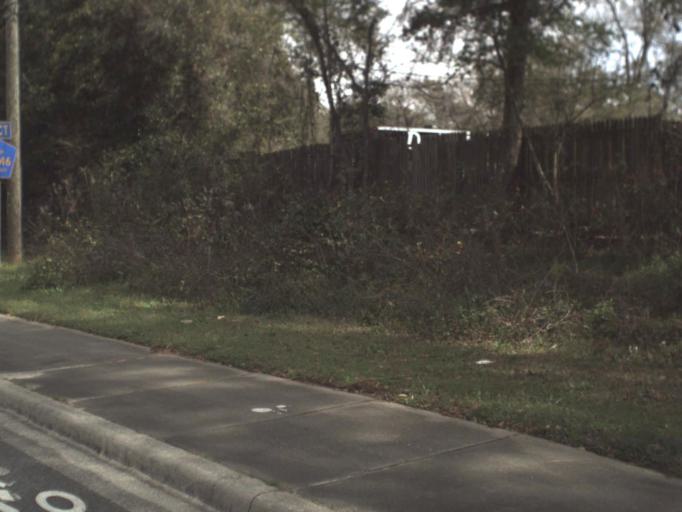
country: US
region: Florida
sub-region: Leon County
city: Tallahassee
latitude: 30.5354
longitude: -84.2316
